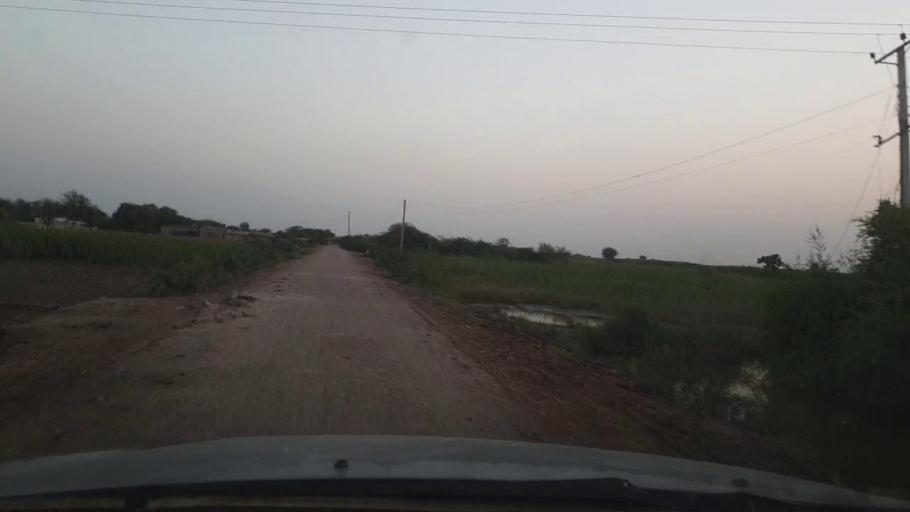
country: PK
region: Sindh
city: Digri
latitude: 25.1202
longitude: 69.0005
